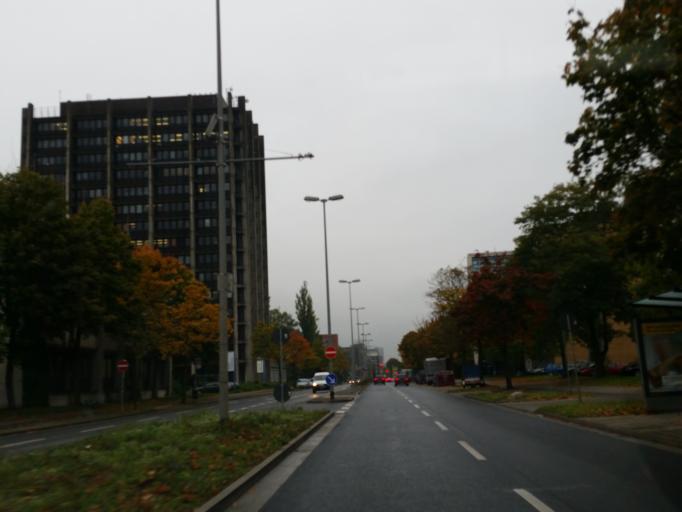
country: DE
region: Lower Saxony
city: Braunschweig
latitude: 52.2770
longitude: 10.5423
